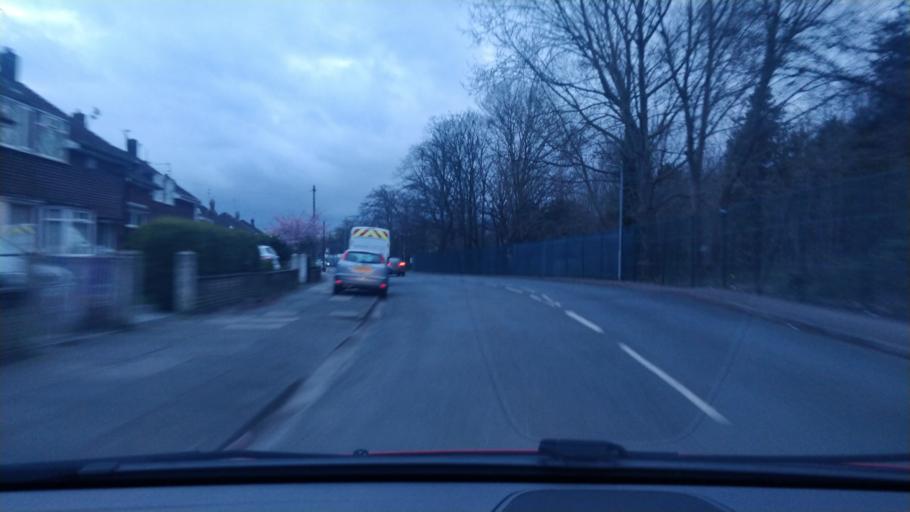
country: GB
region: England
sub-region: Knowsley
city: Knowsley
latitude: 53.4300
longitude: -2.8821
